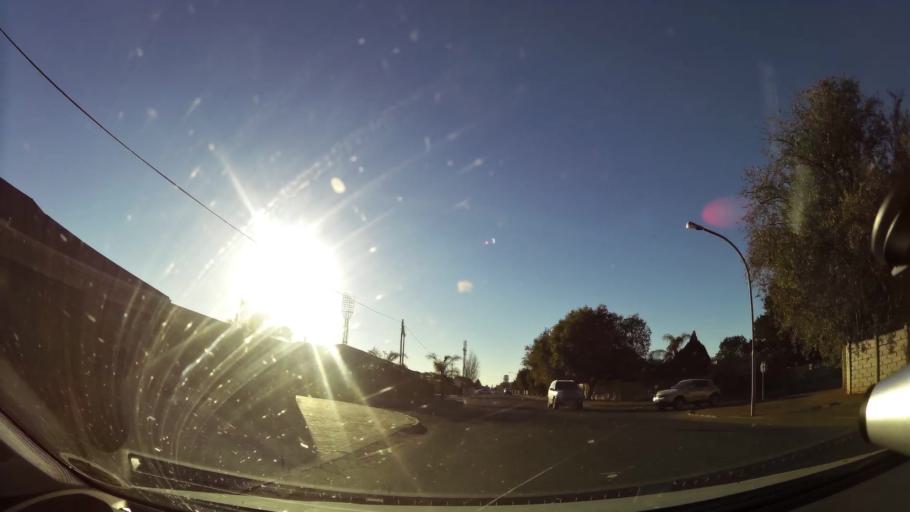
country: ZA
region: Northern Cape
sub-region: Frances Baard District Municipality
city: Kimberley
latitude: -28.7567
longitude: 24.7554
